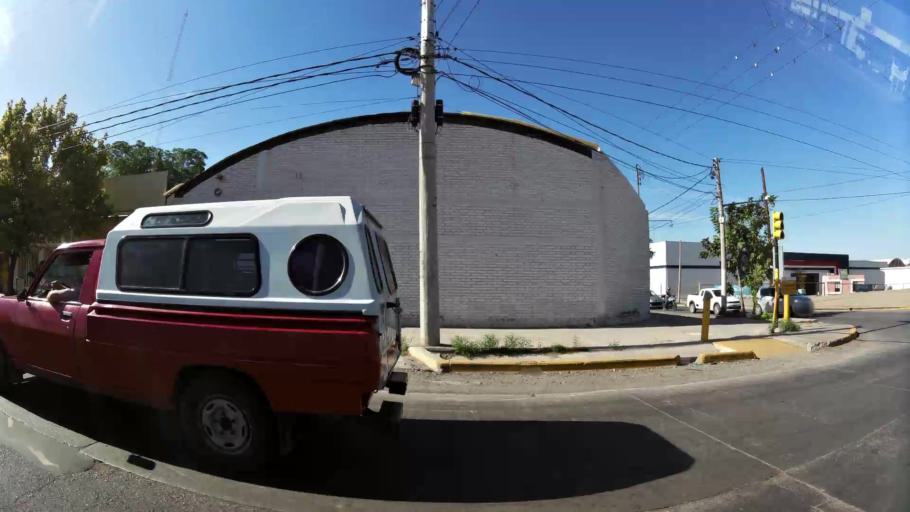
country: AR
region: Mendoza
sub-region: Departamento de Godoy Cruz
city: Godoy Cruz
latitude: -32.9269
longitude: -68.8213
